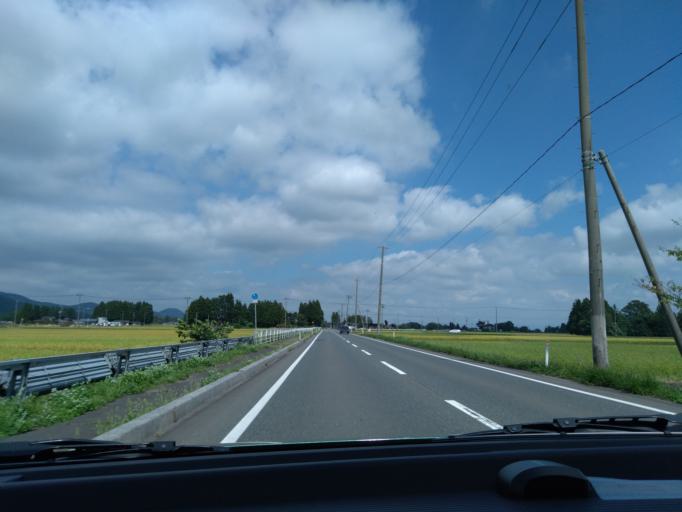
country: JP
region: Iwate
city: Hanamaki
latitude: 39.3954
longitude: 141.0601
